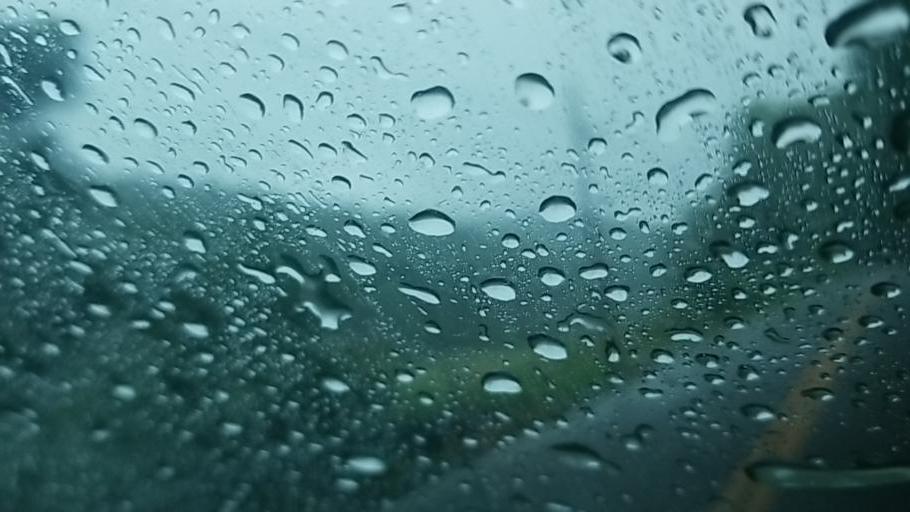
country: US
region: Ohio
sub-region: Holmes County
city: Millersburg
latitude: 40.5298
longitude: -82.0766
